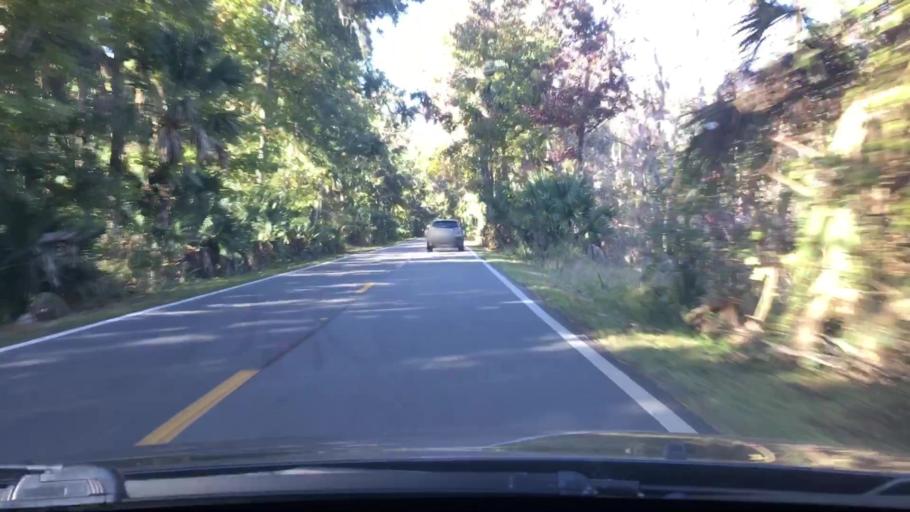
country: US
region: Florida
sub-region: Volusia County
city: Ormond-by-the-Sea
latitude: 29.3709
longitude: -81.1267
